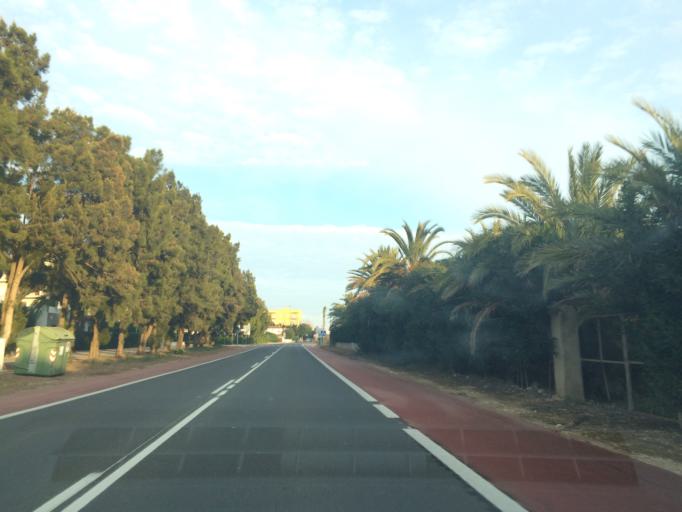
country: ES
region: Valencia
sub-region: Provincia de Alicante
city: els Poblets
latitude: 38.8587
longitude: 0.0453
